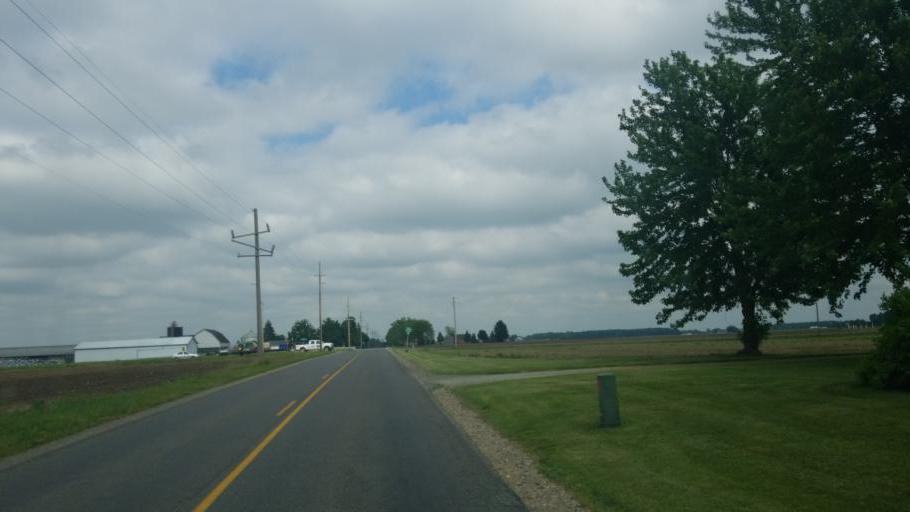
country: US
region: Indiana
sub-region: Elkhart County
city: Wakarusa
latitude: 41.4935
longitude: -86.0226
